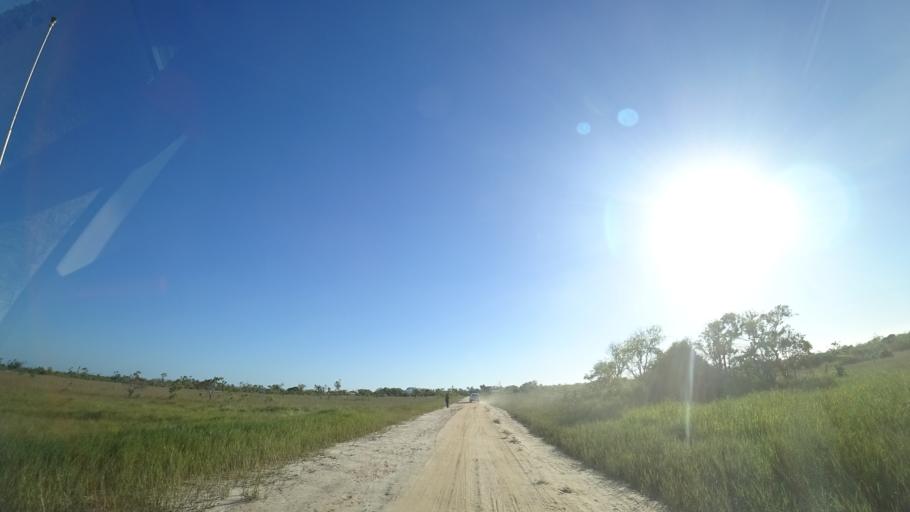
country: MZ
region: Sofala
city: Beira
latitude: -19.5729
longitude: 35.2299
